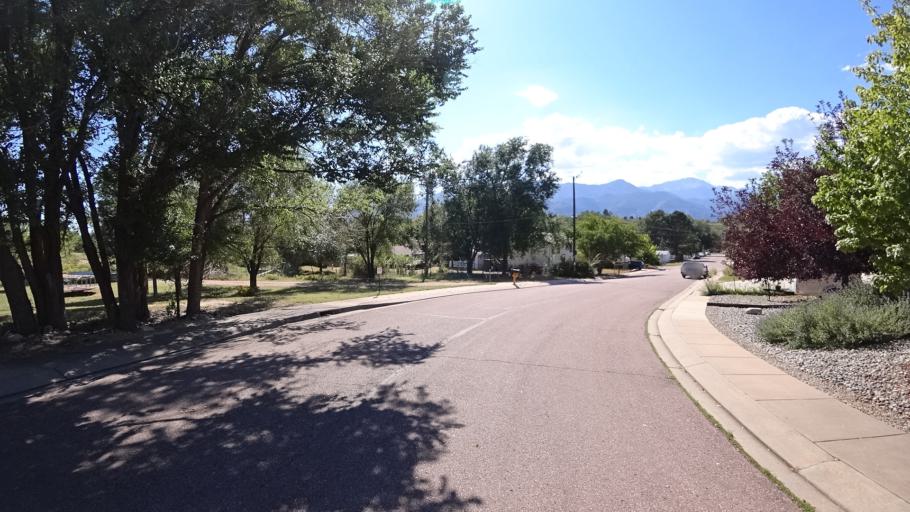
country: US
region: Colorado
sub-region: El Paso County
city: Colorado Springs
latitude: 38.8536
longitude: -104.8470
